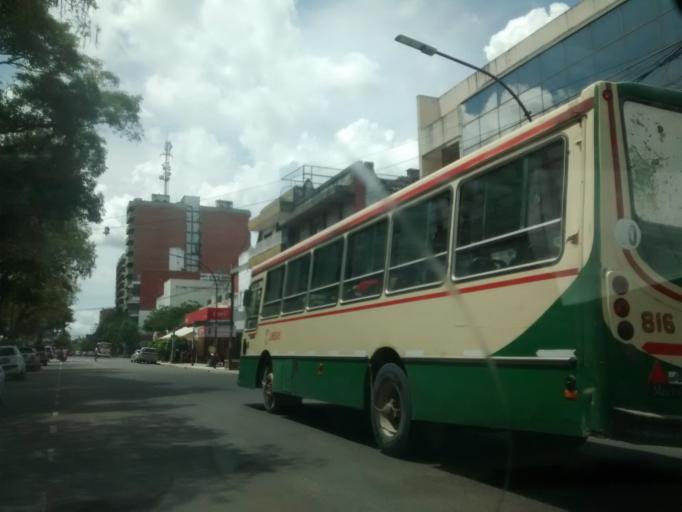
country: AR
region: Chaco
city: Resistencia
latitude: -27.4513
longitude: -58.9881
